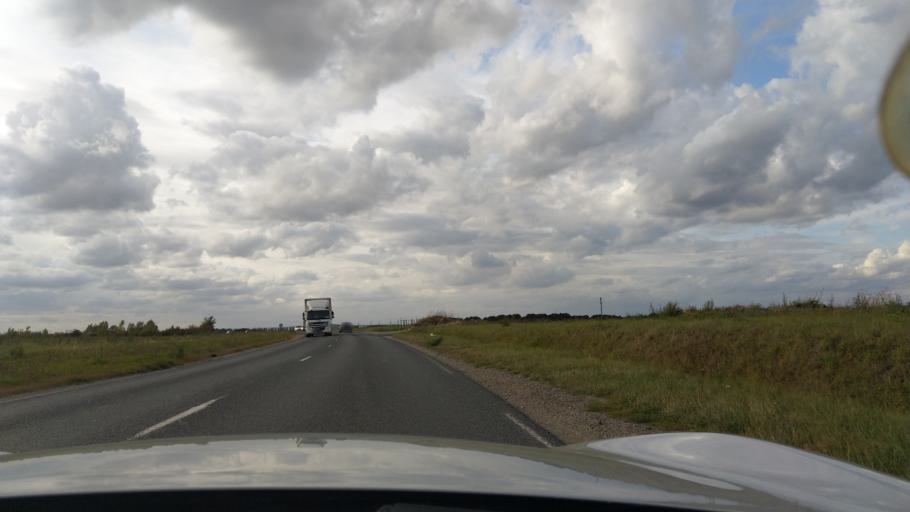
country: FR
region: Ile-de-France
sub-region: Departement du Val-d'Oise
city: Vemars
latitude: 49.0292
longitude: 2.5786
